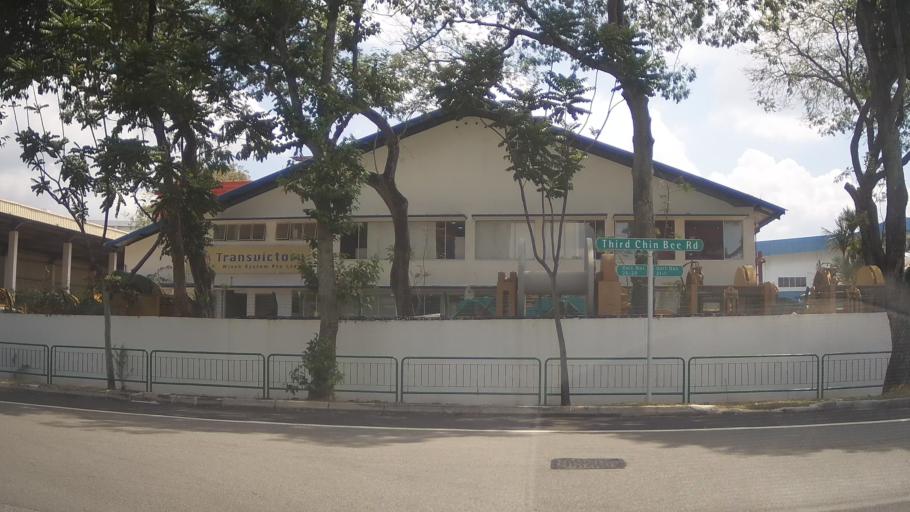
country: MY
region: Johor
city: Johor Bahru
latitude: 1.3343
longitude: 103.7154
